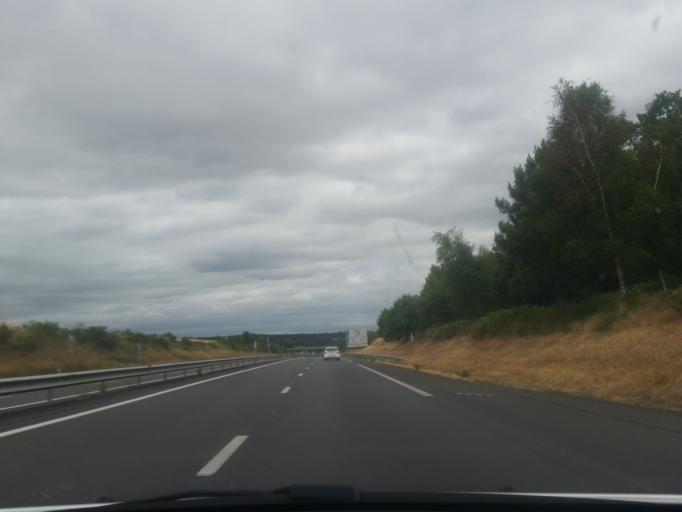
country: FR
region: Pays de la Loire
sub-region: Departement de Maine-et-Loire
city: Durtal
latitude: 47.6392
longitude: -0.2745
